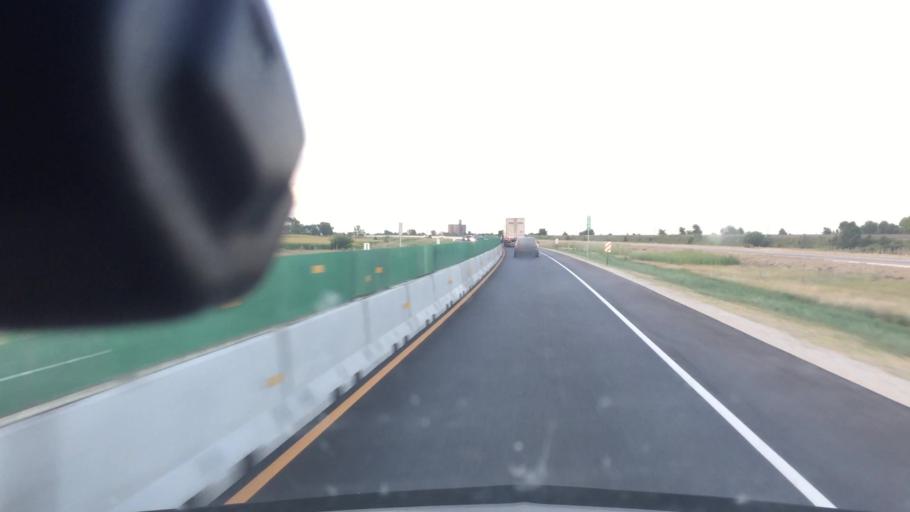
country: US
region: Illinois
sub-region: Livingston County
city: Odell
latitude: 40.9485
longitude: -88.5792
